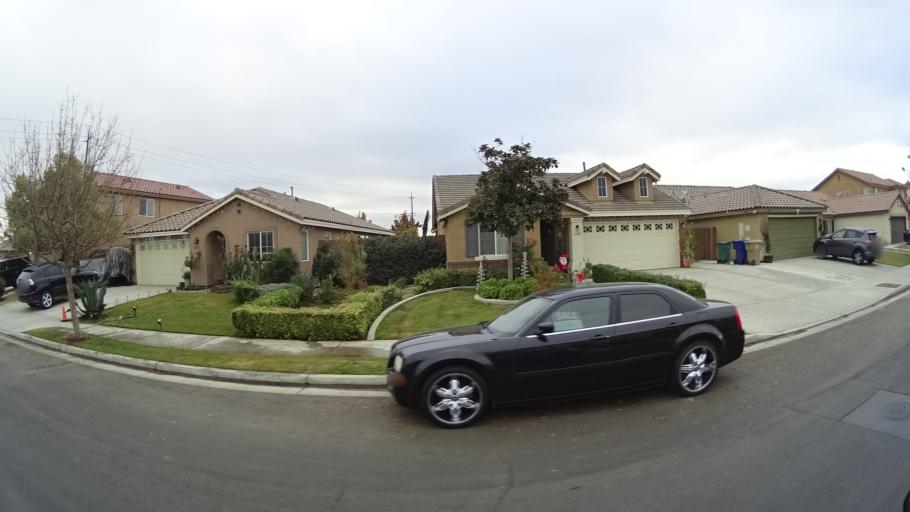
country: US
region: California
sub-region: Kern County
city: Greenfield
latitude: 35.2967
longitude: -119.0714
